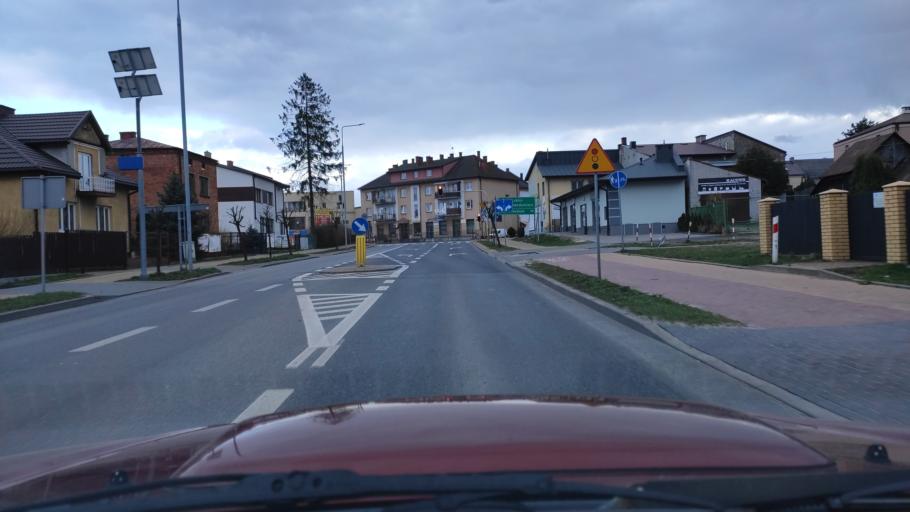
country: PL
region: Masovian Voivodeship
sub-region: Powiat zwolenski
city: Zwolen
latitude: 51.3583
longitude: 21.5822
